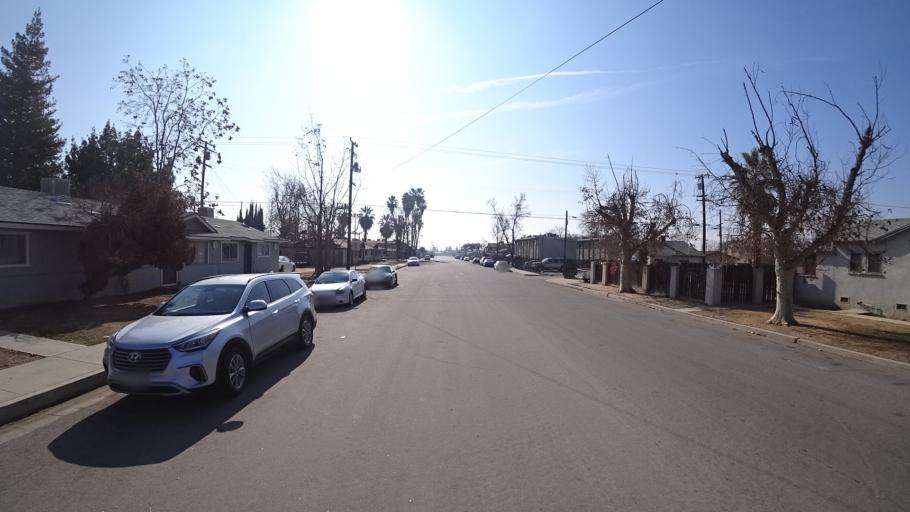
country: US
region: California
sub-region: Kern County
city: Bakersfield
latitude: 35.3829
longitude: -118.9957
